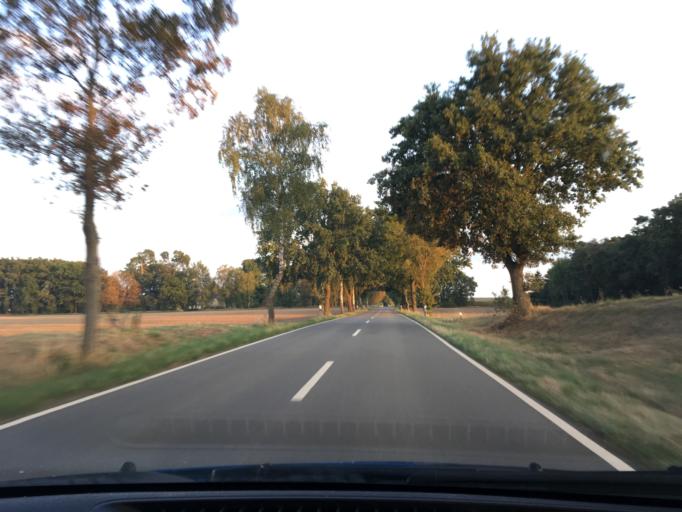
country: DE
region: Lower Saxony
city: Tosterglope
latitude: 53.2173
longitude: 10.8139
